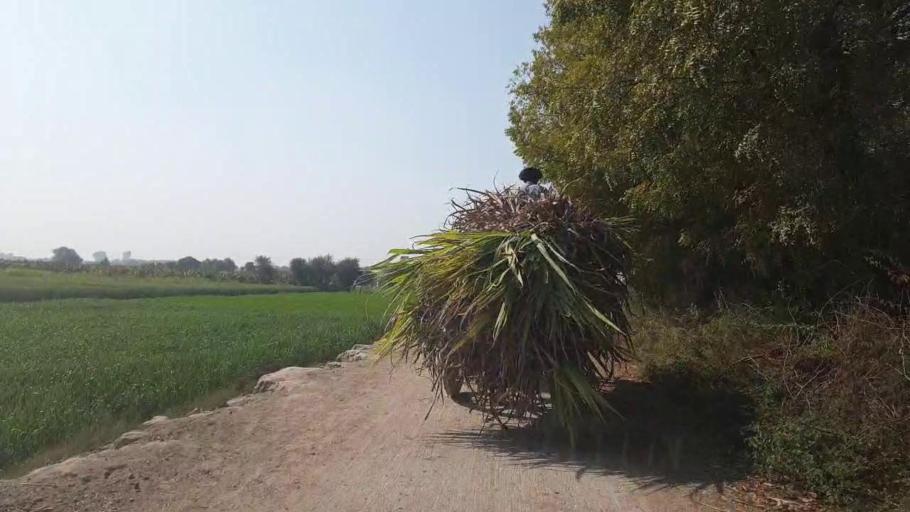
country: PK
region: Sindh
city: Tando Allahyar
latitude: 25.5913
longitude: 68.7522
